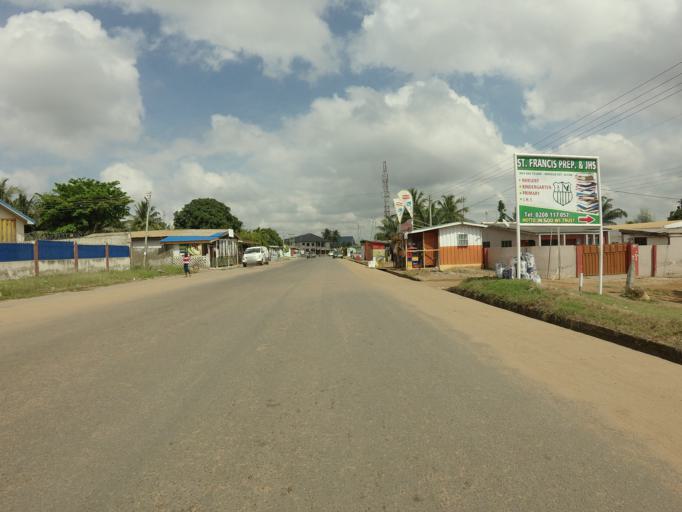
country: GH
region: Greater Accra
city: Nungua
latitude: 5.6147
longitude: -0.0841
